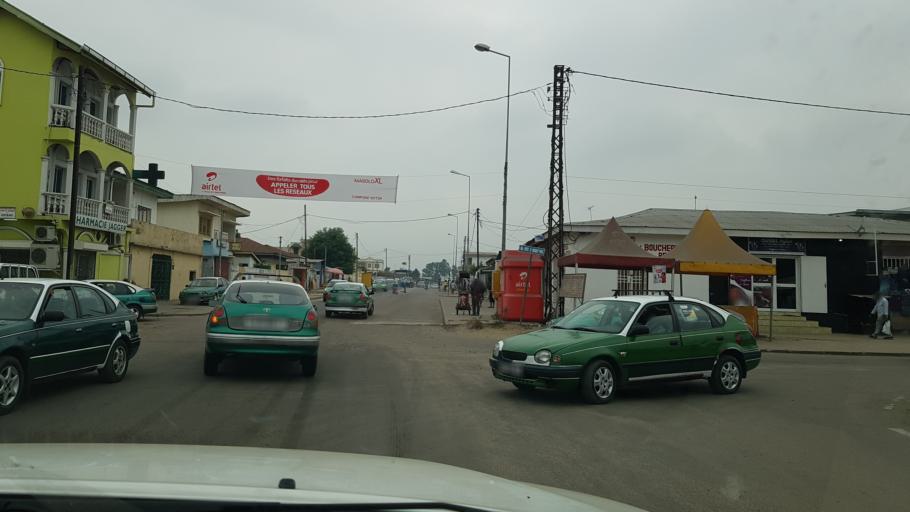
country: CG
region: Brazzaville
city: Brazzaville
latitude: -4.2617
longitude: 15.2606
